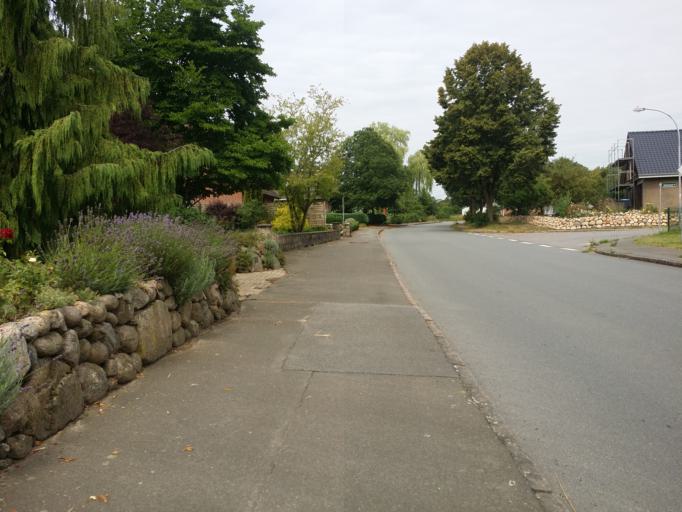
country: DE
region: Schleswig-Holstein
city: Huje
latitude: 53.9787
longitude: 9.4329
